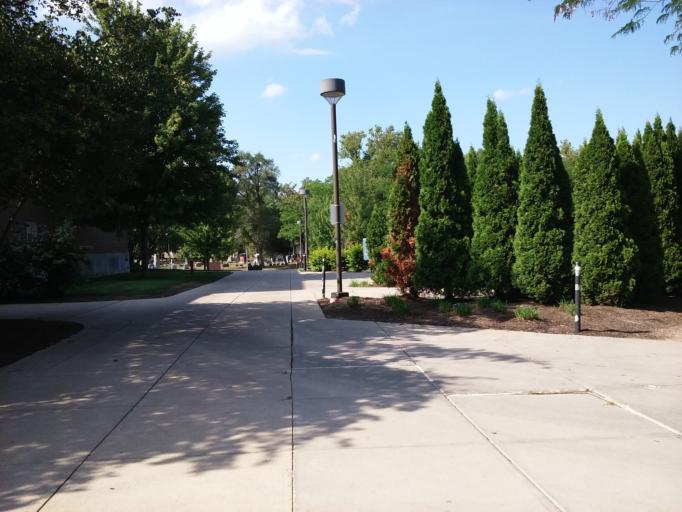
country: US
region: Ohio
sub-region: Wood County
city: Bowling Green
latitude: 41.3773
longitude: -83.6370
